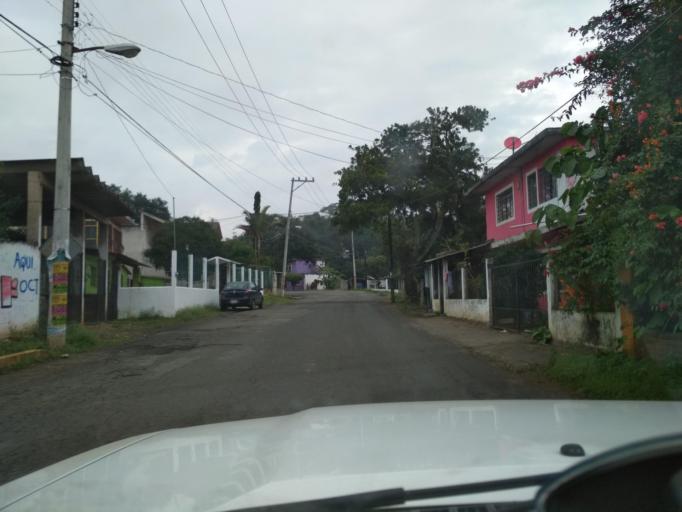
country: MX
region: Veracruz
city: El Castillo
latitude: 19.5654
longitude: -96.8654
